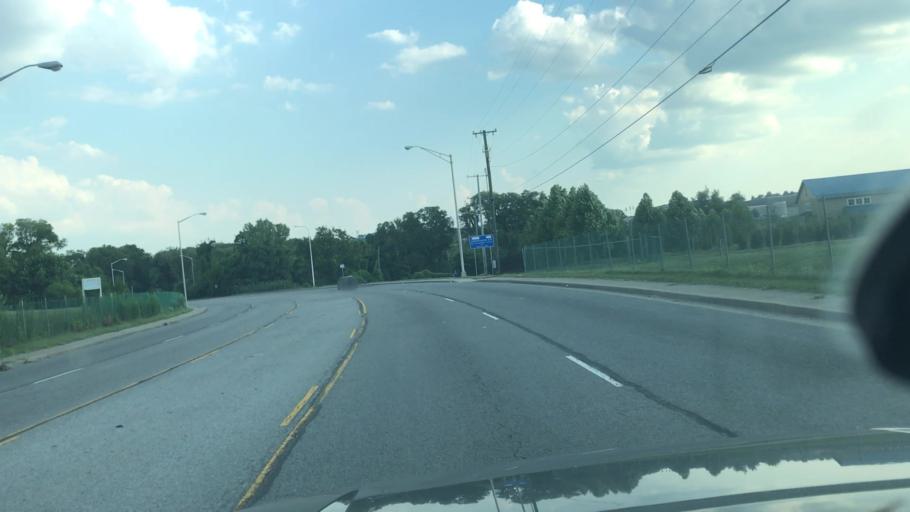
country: US
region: Tennessee
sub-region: Davidson County
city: Nashville
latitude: 36.1772
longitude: -86.8246
